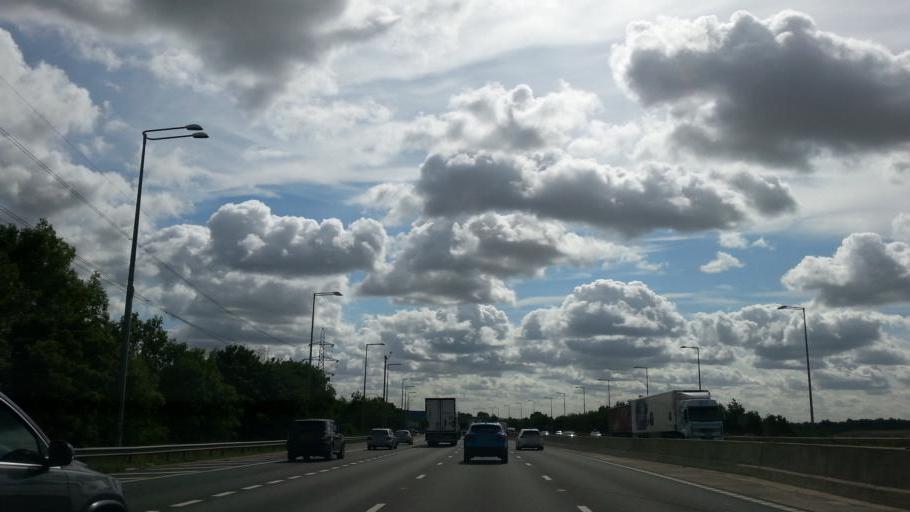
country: GB
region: England
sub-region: Essex
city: Theydon Bois
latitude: 51.6832
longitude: 0.1087
